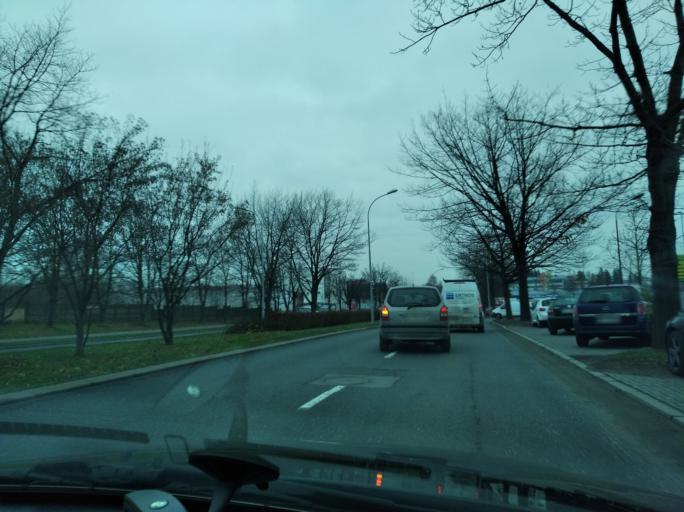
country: PL
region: Subcarpathian Voivodeship
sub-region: Rzeszow
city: Rzeszow
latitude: 50.0535
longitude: 21.9887
